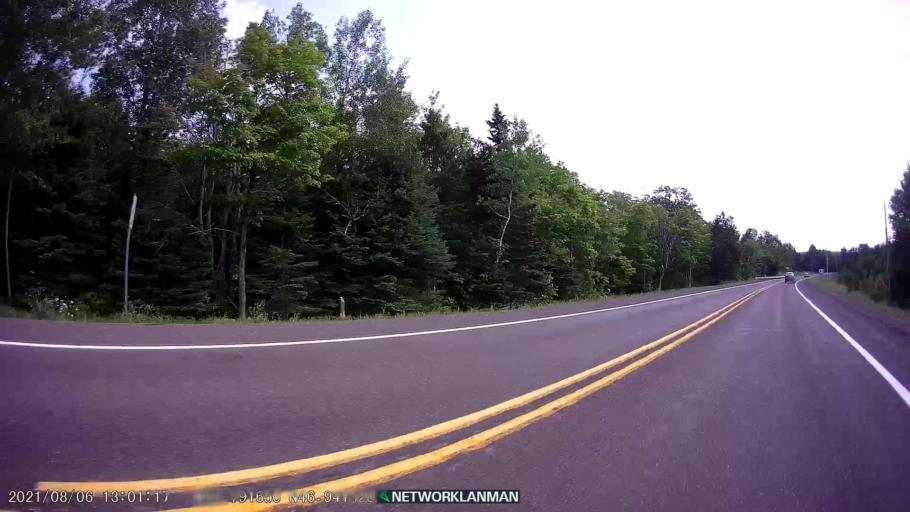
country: US
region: Michigan
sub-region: Houghton County
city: Hancock
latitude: 46.9413
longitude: -88.7918
